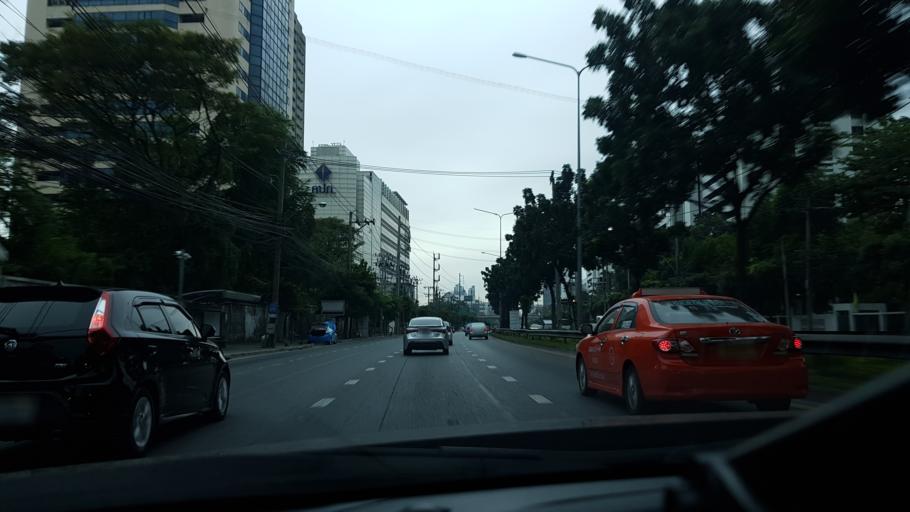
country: TH
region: Bangkok
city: Chatuchak
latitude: 13.8185
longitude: 100.5756
